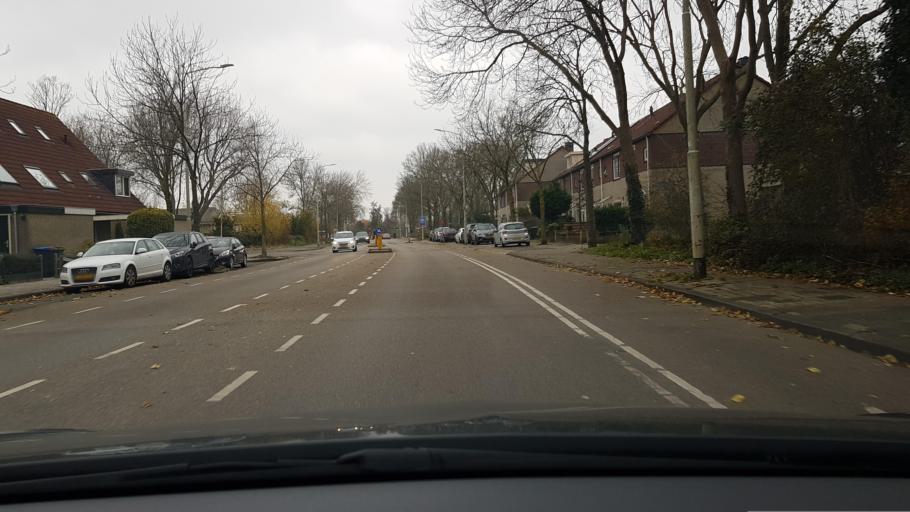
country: NL
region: North Holland
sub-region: Gemeente Haarlem
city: Haarlem
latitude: 52.3657
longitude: 4.6645
